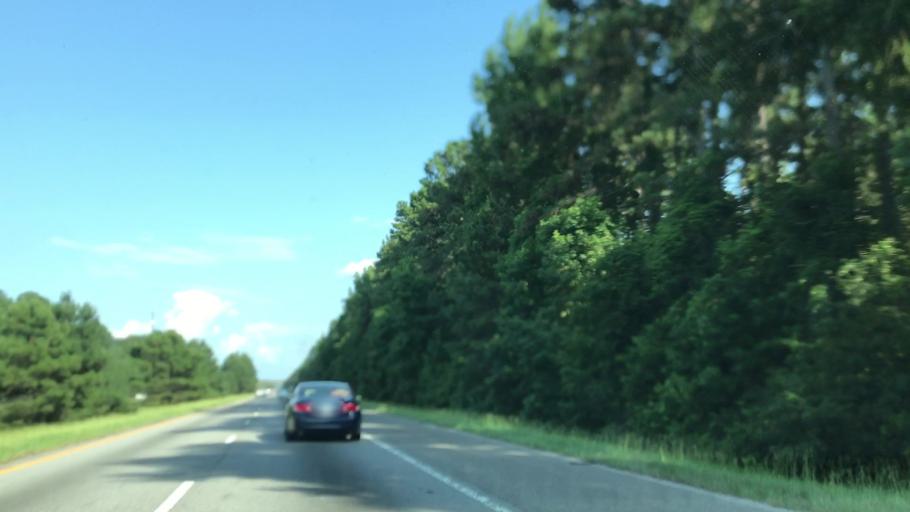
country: US
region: South Carolina
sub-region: Orangeburg County
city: Brookdale
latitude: 33.4294
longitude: -80.6907
